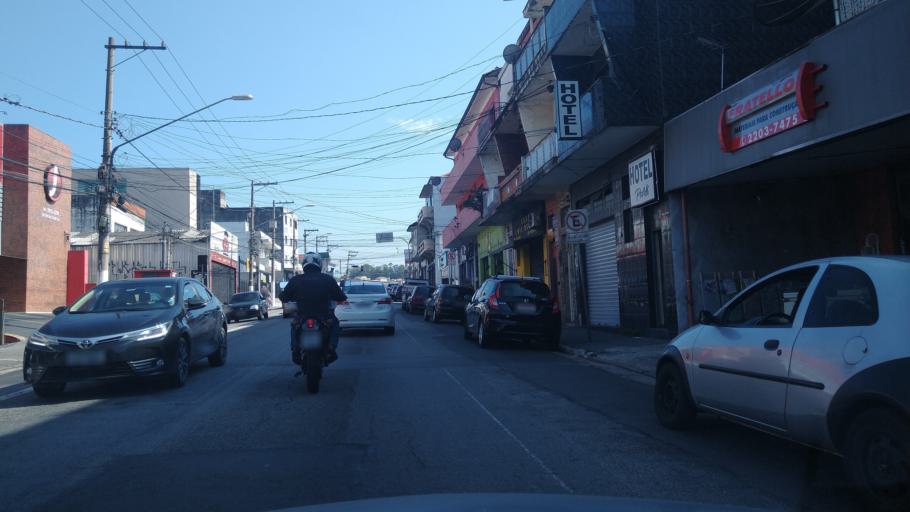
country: BR
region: Sao Paulo
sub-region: Sao Paulo
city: Sao Paulo
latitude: -23.4810
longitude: -46.6219
